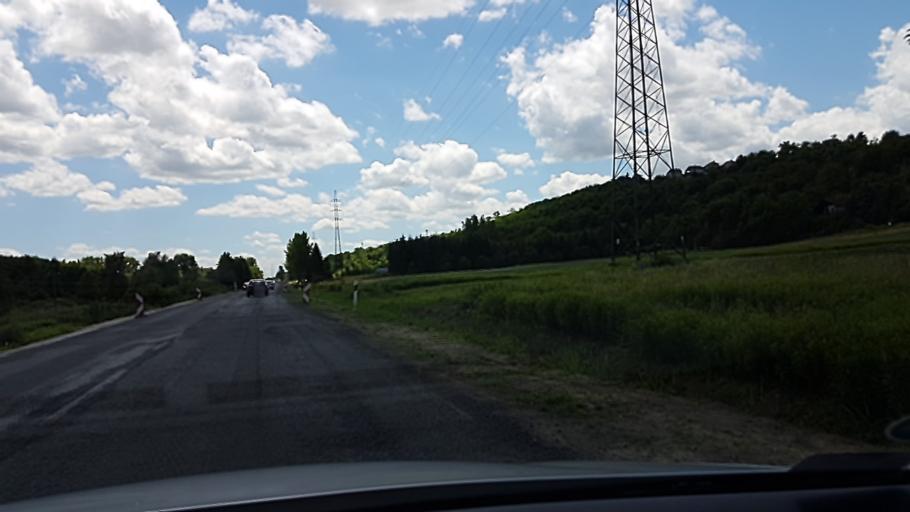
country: HU
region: Zala
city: Zalaegerszeg
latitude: 46.8269
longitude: 16.8634
